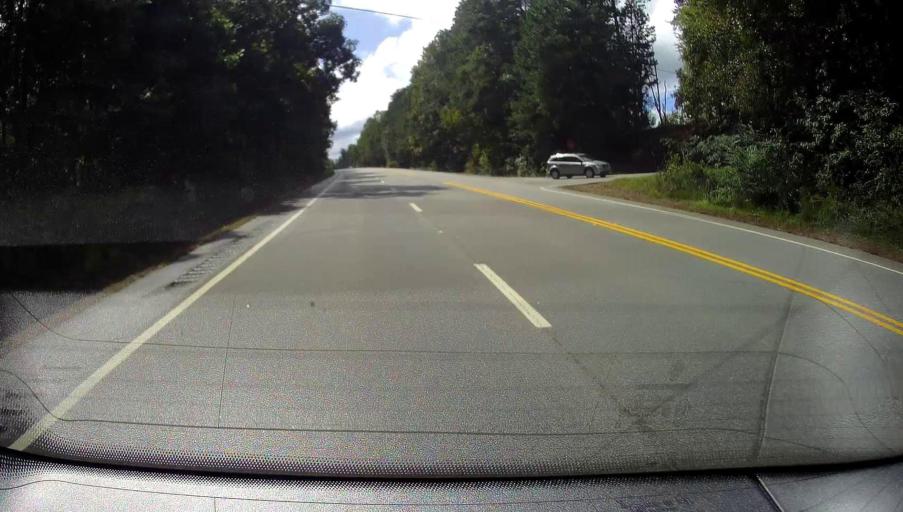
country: US
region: Georgia
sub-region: Baldwin County
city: Milledgeville
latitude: 33.0520
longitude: -83.2890
